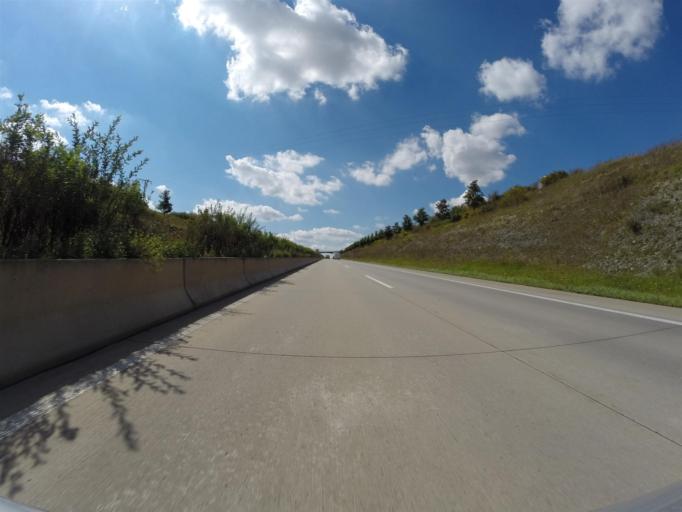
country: DE
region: Thuringia
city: Elxleben
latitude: 51.0082
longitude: 10.9466
